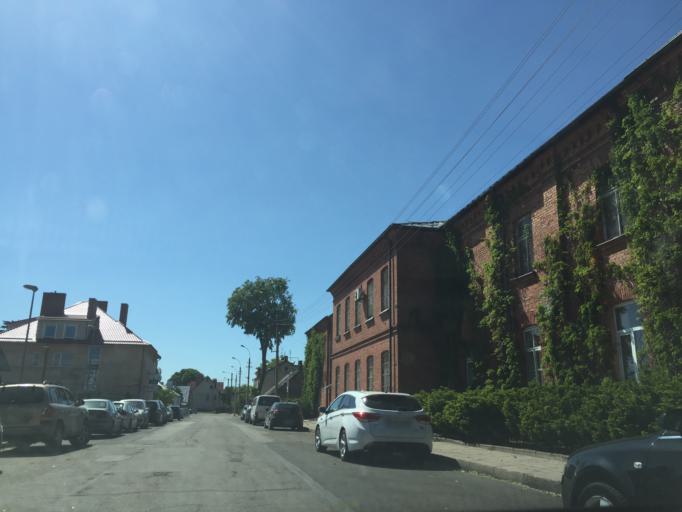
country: LT
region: Panevezys
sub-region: Panevezys City
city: Panevezys
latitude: 55.7334
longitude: 24.3554
